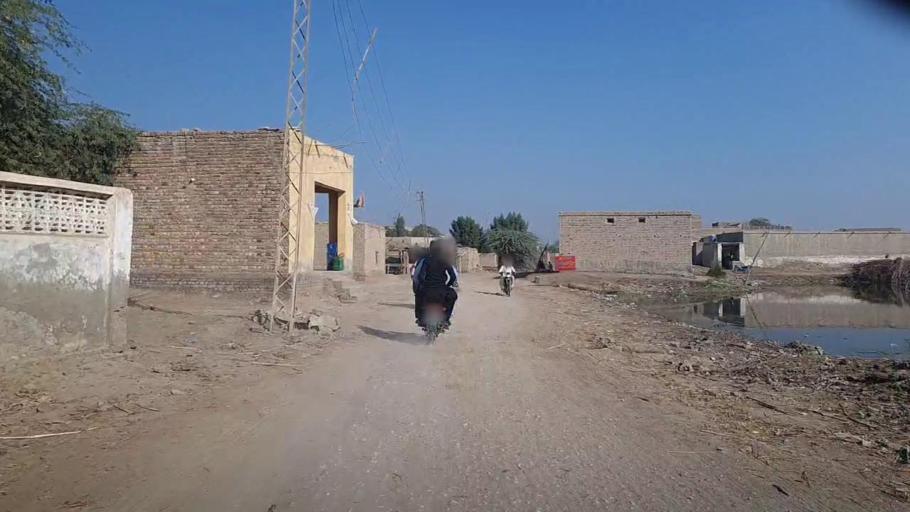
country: PK
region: Sindh
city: Darya Khan Marri
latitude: 26.6723
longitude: 68.3210
